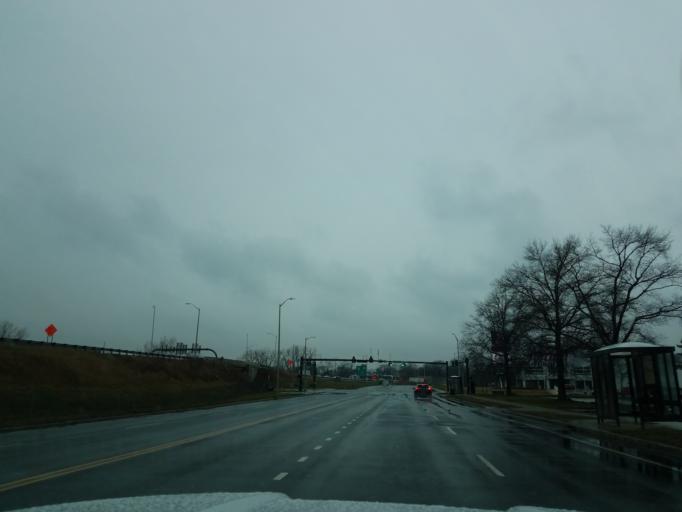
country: US
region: Connecticut
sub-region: New Haven County
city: New Haven
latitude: 41.2882
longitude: -72.9250
